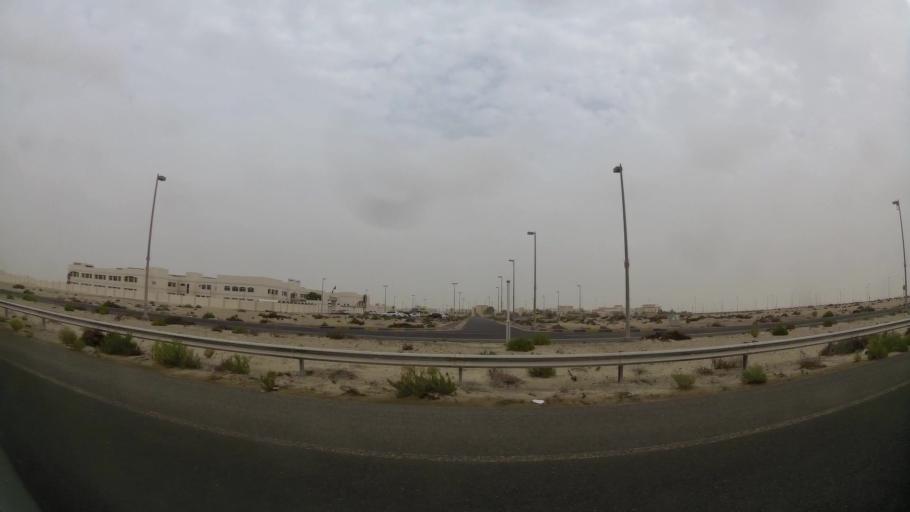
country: AE
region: Abu Dhabi
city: Abu Dhabi
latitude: 24.3902
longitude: 54.7369
